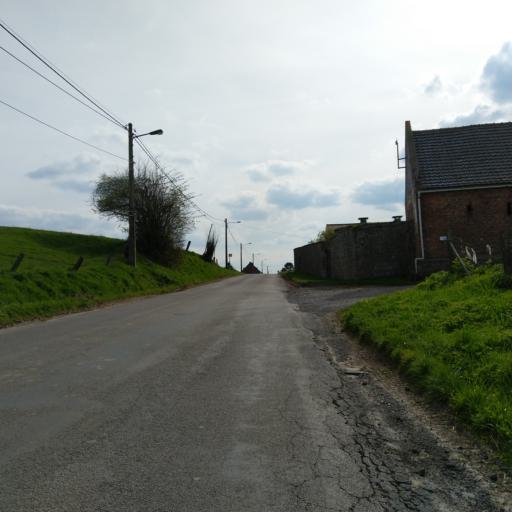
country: BE
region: Wallonia
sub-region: Province du Hainaut
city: Jurbise
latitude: 50.5297
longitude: 3.9669
